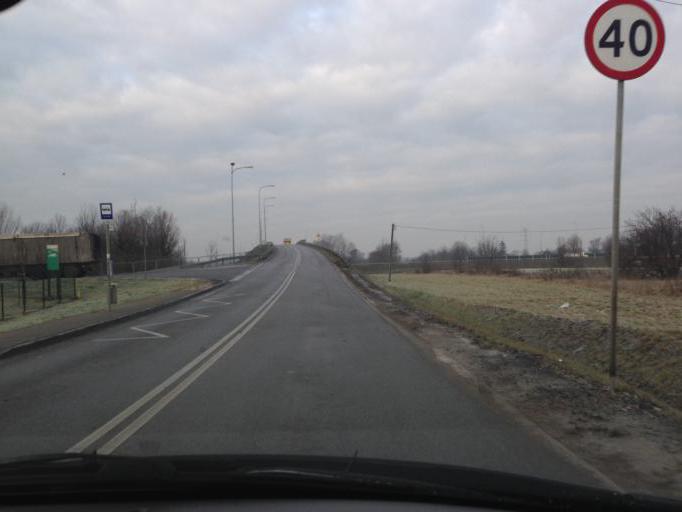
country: PL
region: Lesser Poland Voivodeship
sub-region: Powiat wielicki
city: Kokotow
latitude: 50.0594
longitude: 20.0787
